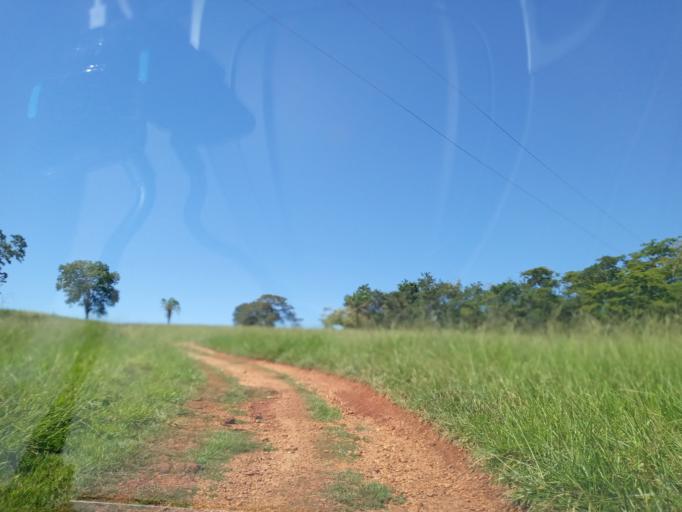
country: BR
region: Goias
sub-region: Itumbiara
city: Itumbiara
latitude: -18.4031
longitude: -49.1422
